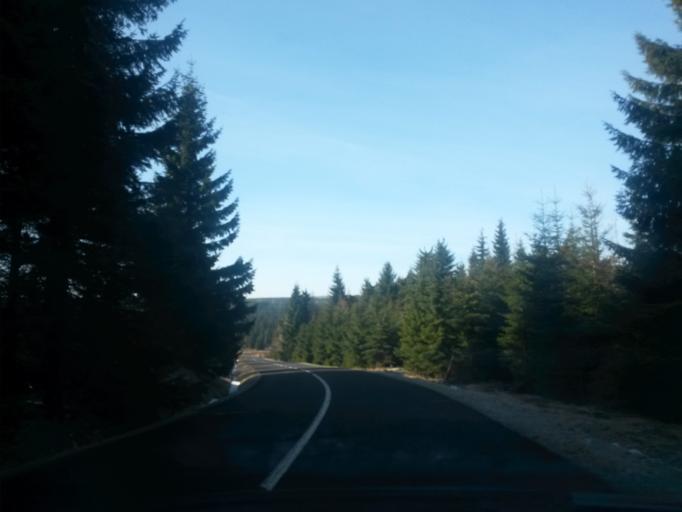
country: CZ
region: Ustecky
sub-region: Okres Chomutov
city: Kovarska
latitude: 50.4093
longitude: 13.0312
